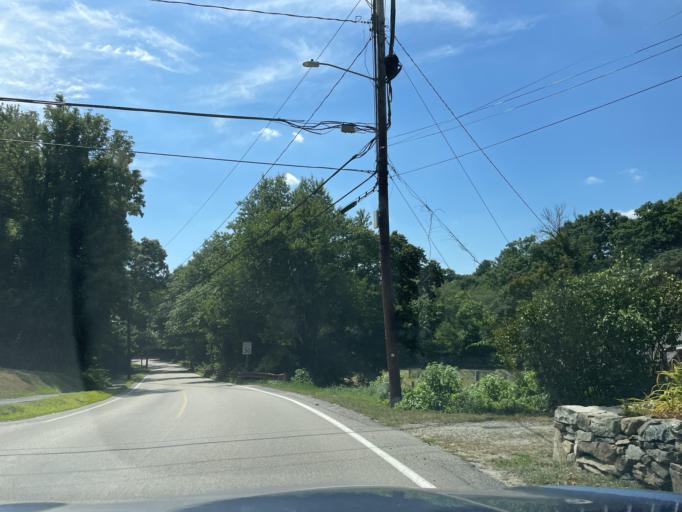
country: US
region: Massachusetts
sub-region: Middlesex County
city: Sherborn
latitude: 42.2377
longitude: -71.3953
